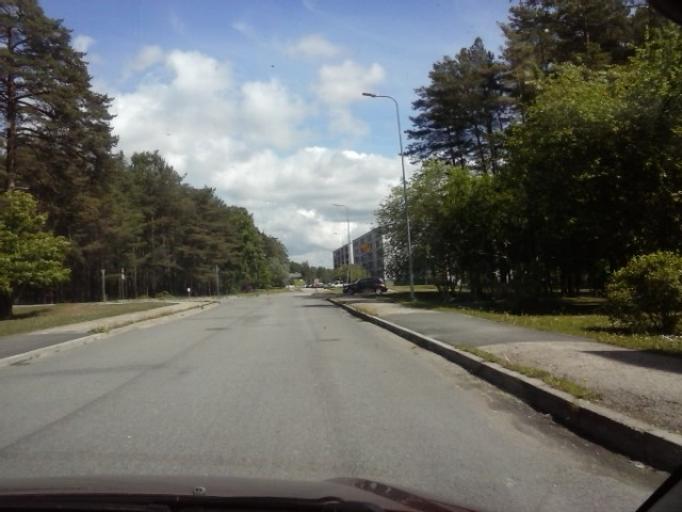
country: EE
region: Laeaene
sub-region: Haapsalu linn
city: Haapsalu
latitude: 58.9341
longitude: 23.5557
